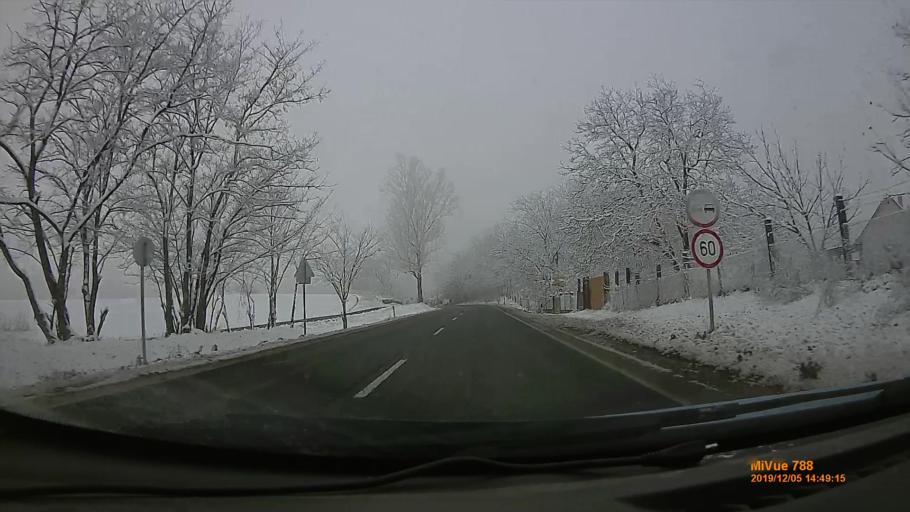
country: HU
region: Szabolcs-Szatmar-Bereg
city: Nyiregyhaza
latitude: 47.9827
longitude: 21.6795
